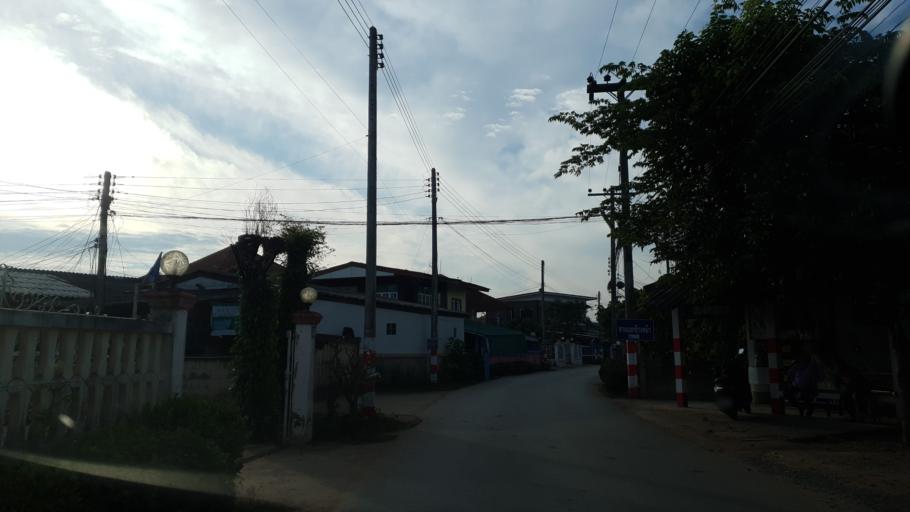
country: TH
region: Lamphun
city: Lamphun
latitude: 18.5235
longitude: 99.0179
